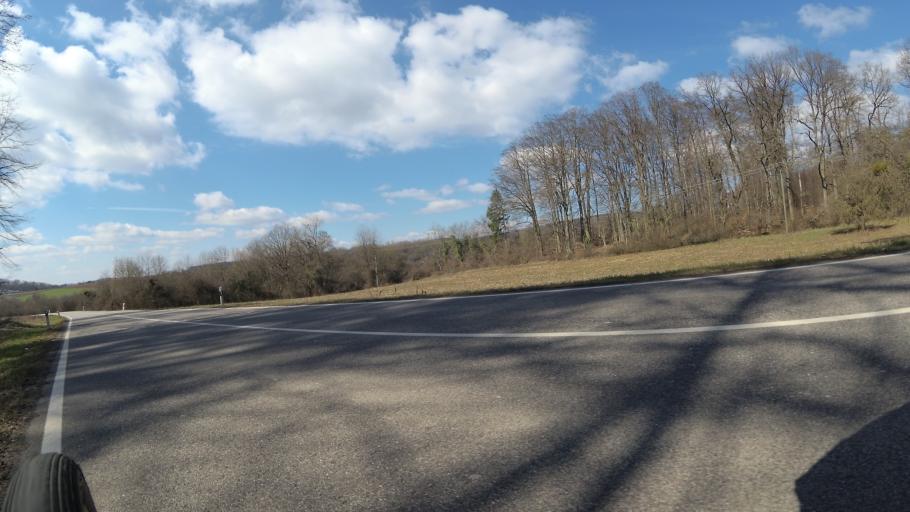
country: DE
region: Saarland
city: Rehlingen-Siersburg
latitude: 49.3581
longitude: 6.6460
